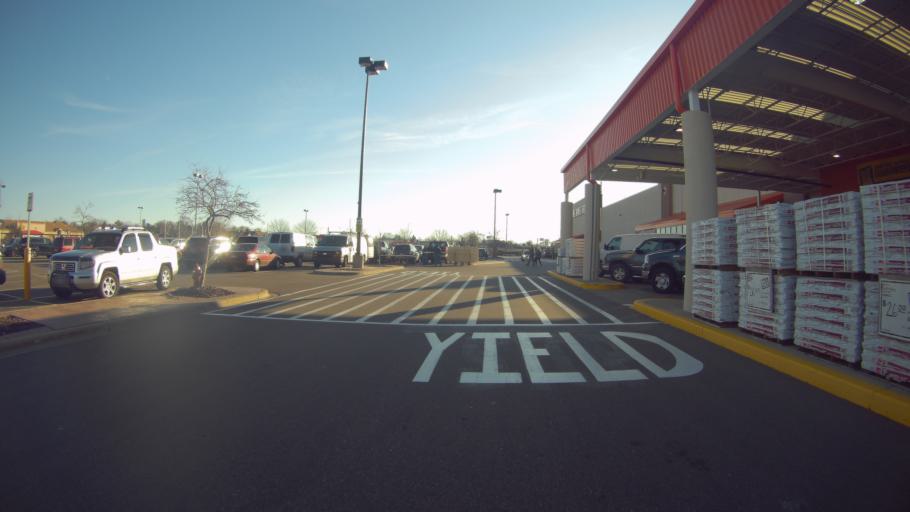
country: US
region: Wisconsin
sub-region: Dane County
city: Shorewood Hills
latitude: 43.0368
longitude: -89.4566
